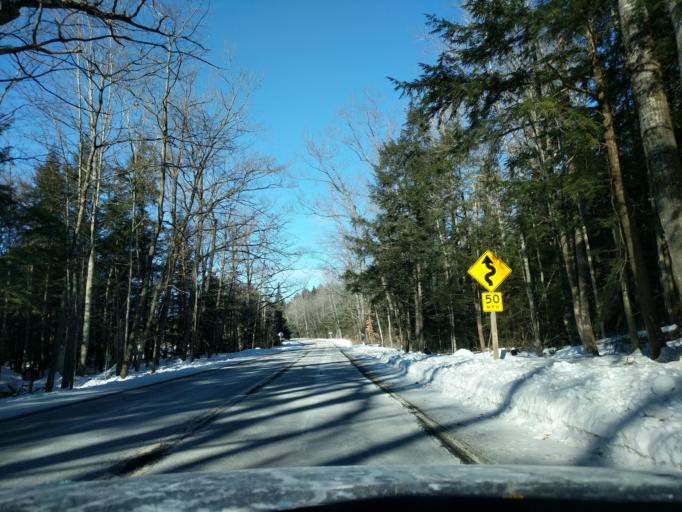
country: US
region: Wisconsin
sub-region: Menominee County
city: Keshena
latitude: 45.1058
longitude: -88.6379
